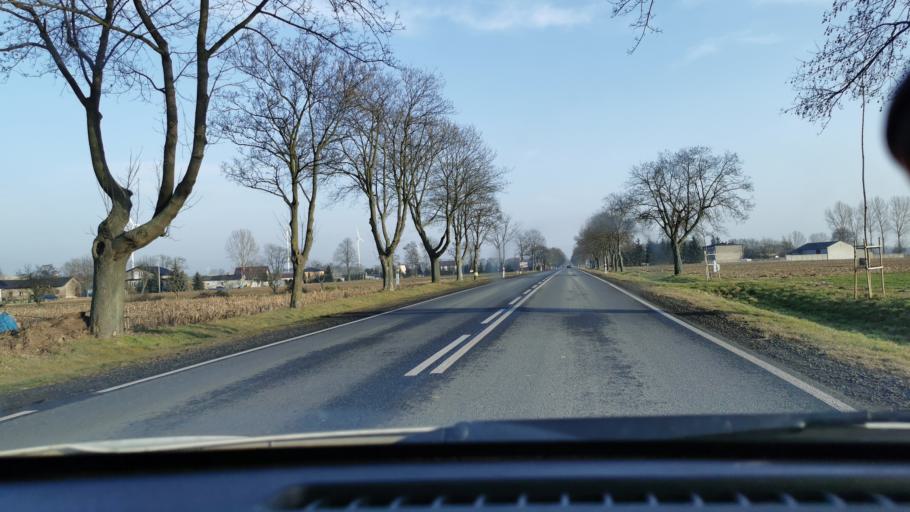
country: PL
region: Lodz Voivodeship
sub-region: Powiat sieradzki
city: Blaszki
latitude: 51.6377
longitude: 18.5169
